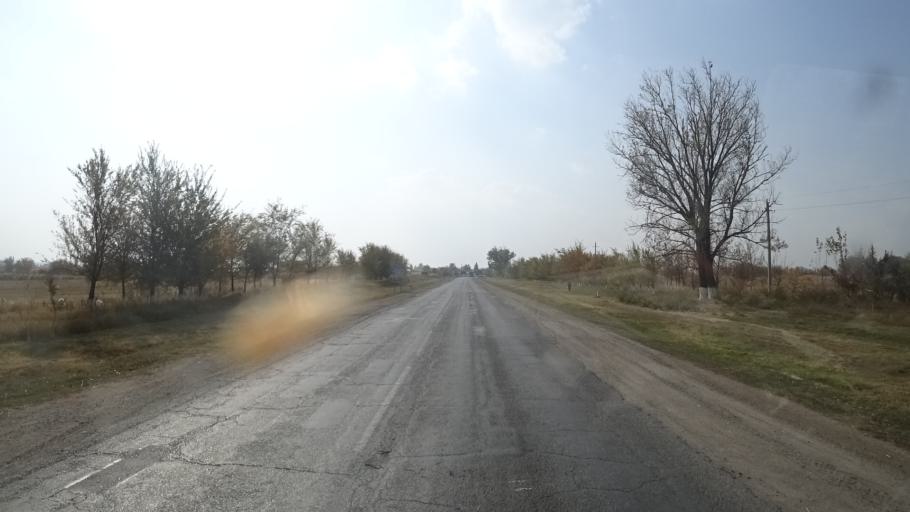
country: KZ
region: Zhambyl
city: Taraz
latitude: 42.9364
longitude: 71.4427
